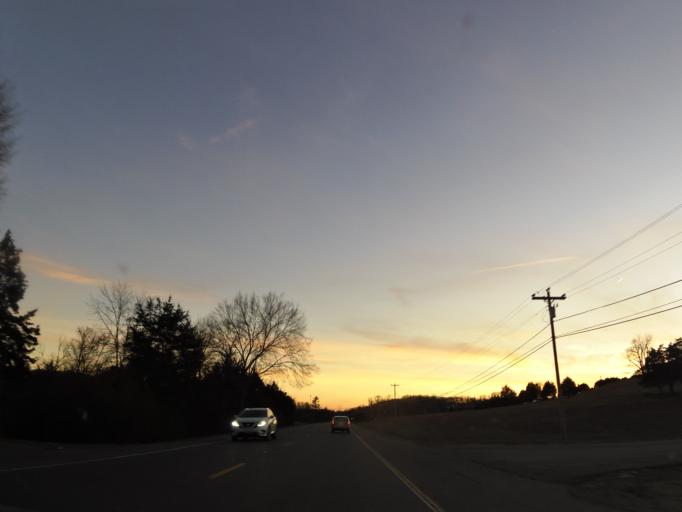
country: US
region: Tennessee
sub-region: Bradley County
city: Wildwood Lake
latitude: 35.0859
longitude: -84.8863
